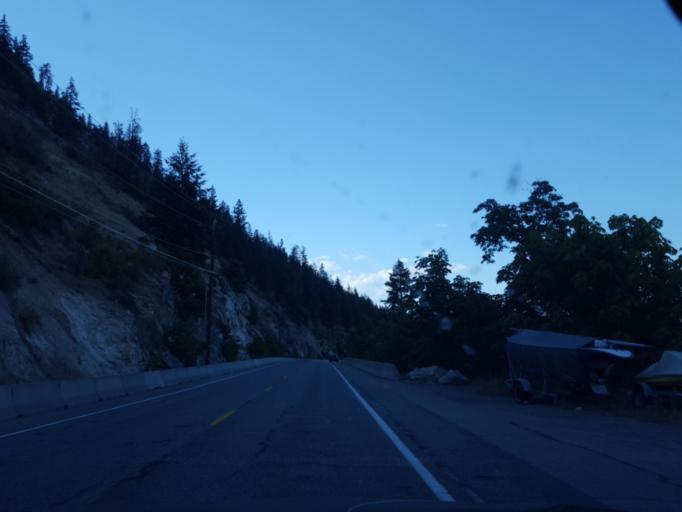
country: US
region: Washington
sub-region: Chelan County
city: Granite Falls
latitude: 47.8919
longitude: -120.2151
